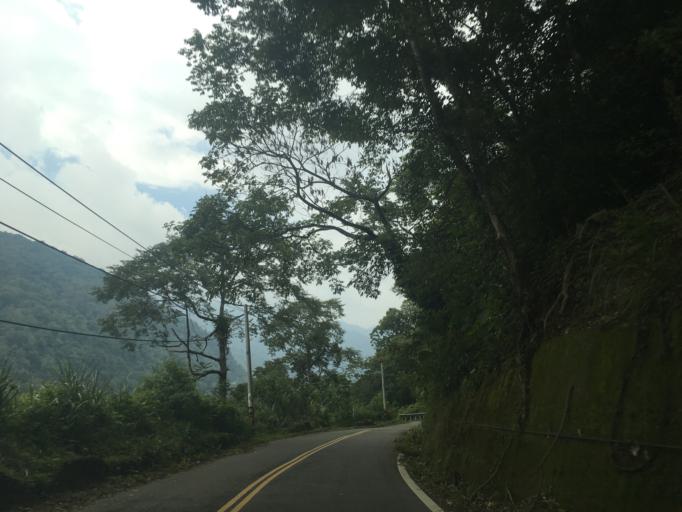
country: TW
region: Taiwan
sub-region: Miaoli
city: Miaoli
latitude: 24.3576
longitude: 120.9562
